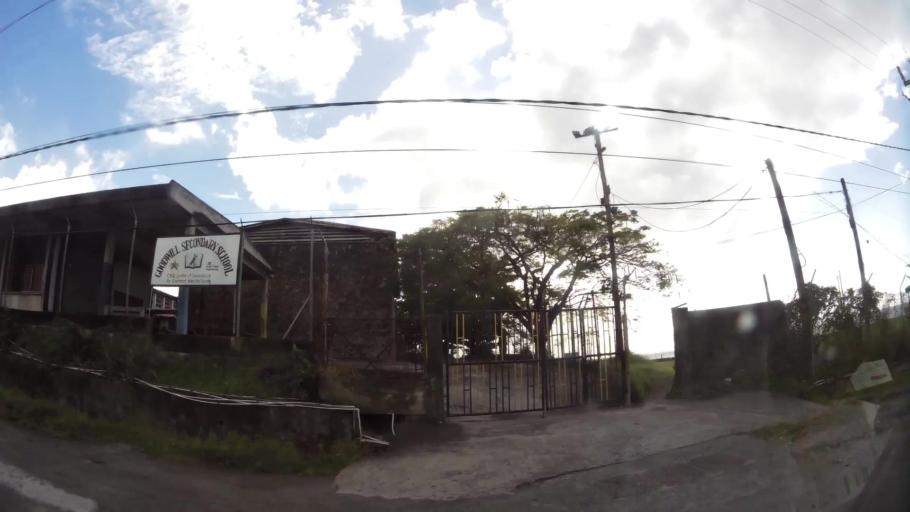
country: DM
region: Saint George
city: Roseau
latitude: 15.3059
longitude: -61.3890
